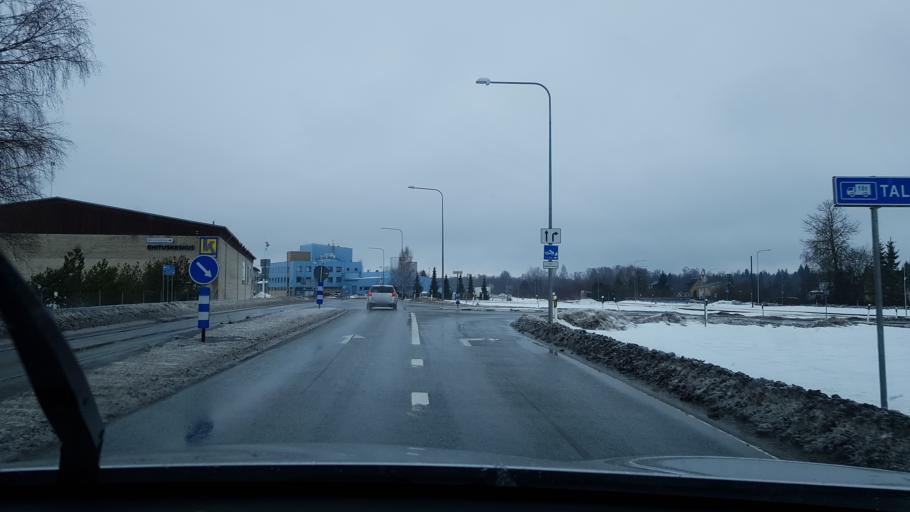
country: EE
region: Raplamaa
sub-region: Rapla vald
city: Rapla
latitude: 58.9896
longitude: 24.8368
